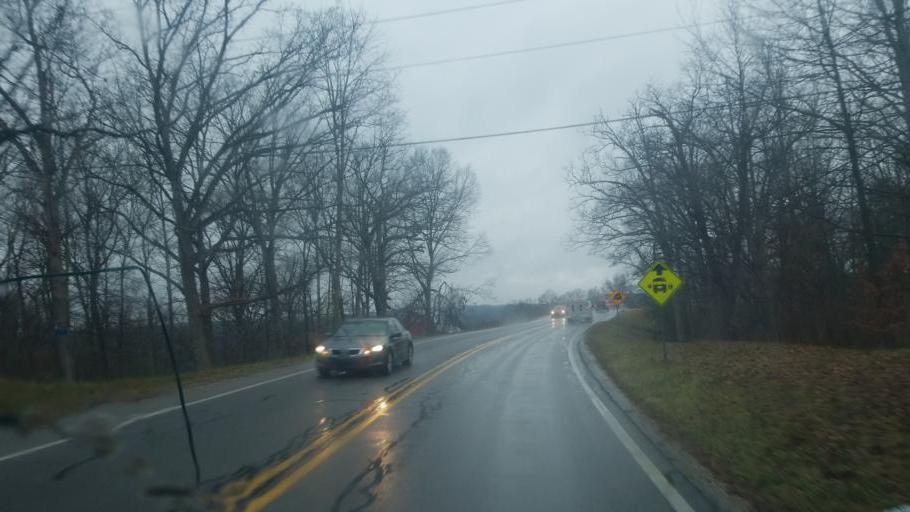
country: US
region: Indiana
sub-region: Brown County
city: Nashville
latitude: 39.1668
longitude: -86.2770
